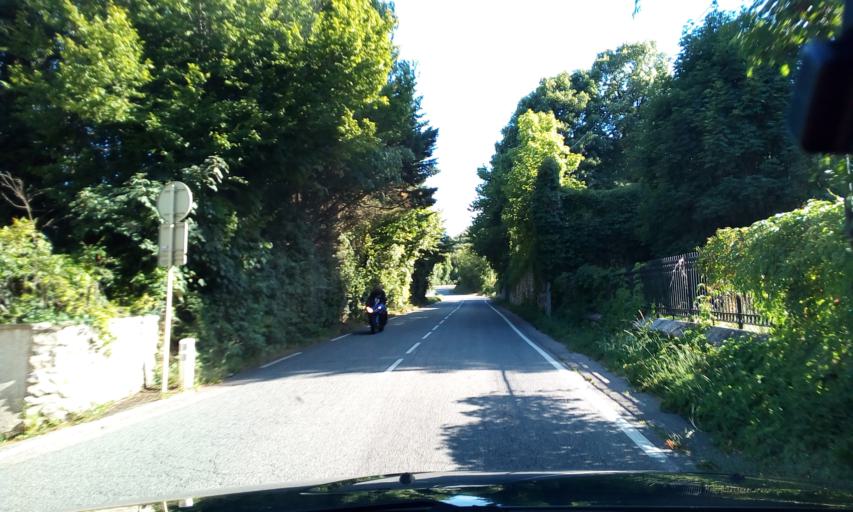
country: FR
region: Rhone-Alpes
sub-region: Departement de l'Isere
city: Seyssins
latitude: 45.1581
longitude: 5.6743
